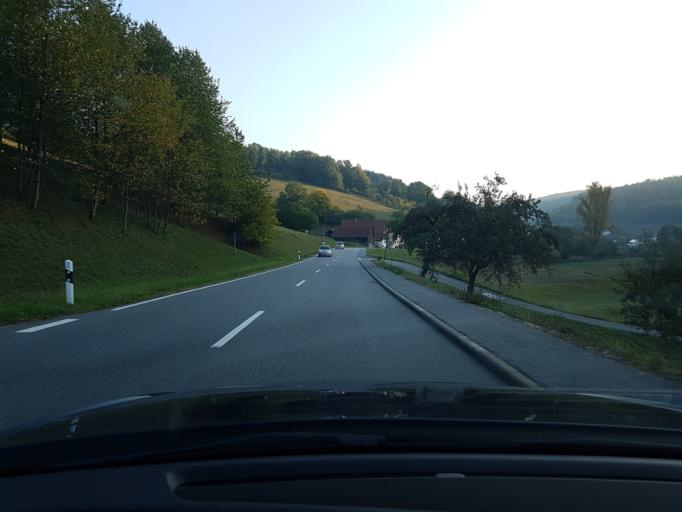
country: DE
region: Hesse
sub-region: Regierungsbezirk Darmstadt
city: Beerfelden
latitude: 49.5383
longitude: 8.9695
